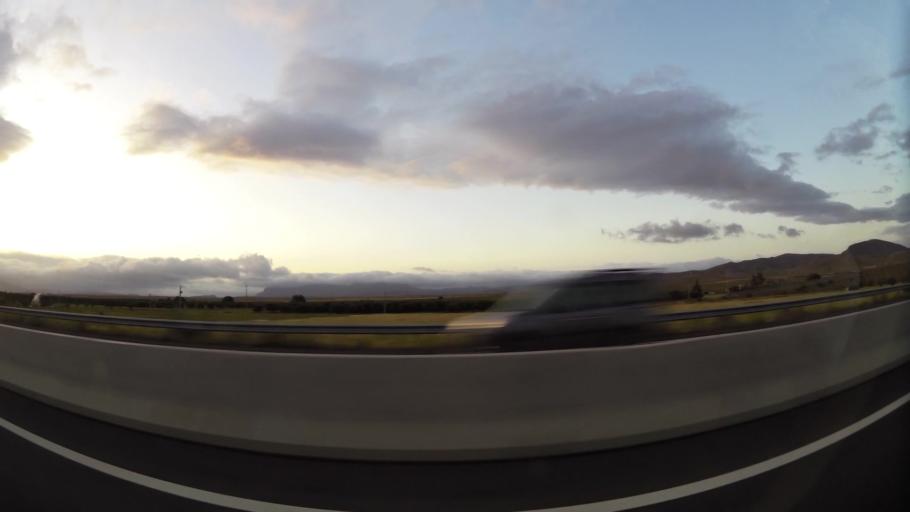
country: MA
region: Oriental
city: El Aioun
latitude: 34.5938
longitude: -2.6974
